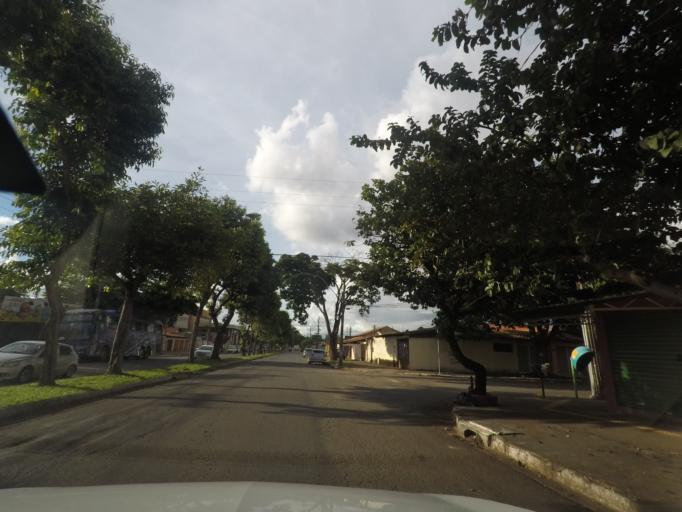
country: BR
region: Goias
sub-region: Goiania
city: Goiania
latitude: -16.6839
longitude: -49.2998
